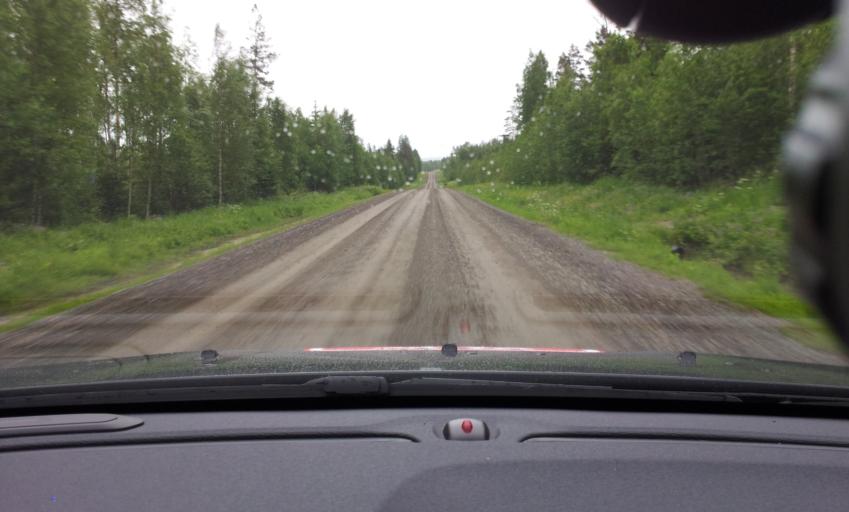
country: SE
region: Jaemtland
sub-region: Ragunda Kommun
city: Hammarstrand
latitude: 63.1345
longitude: 16.3182
